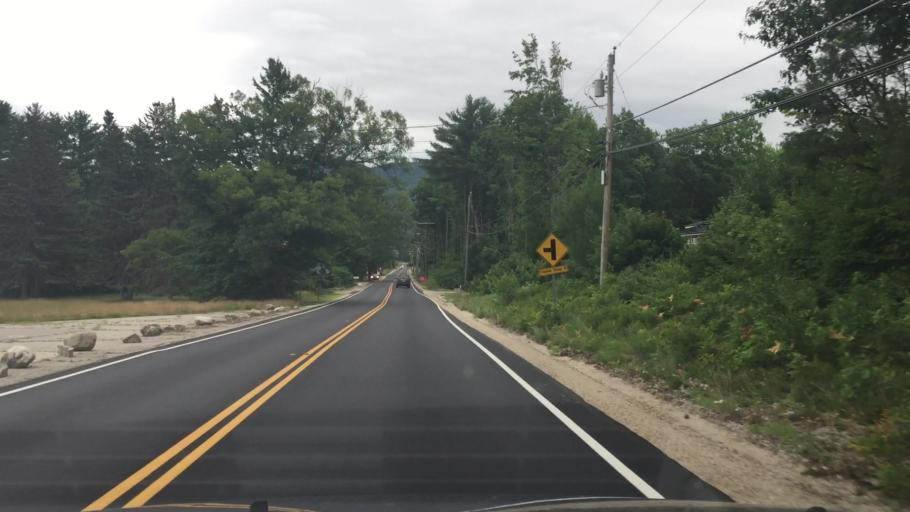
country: US
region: New Hampshire
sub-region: Carroll County
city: Freedom
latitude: 43.8031
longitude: -71.0596
